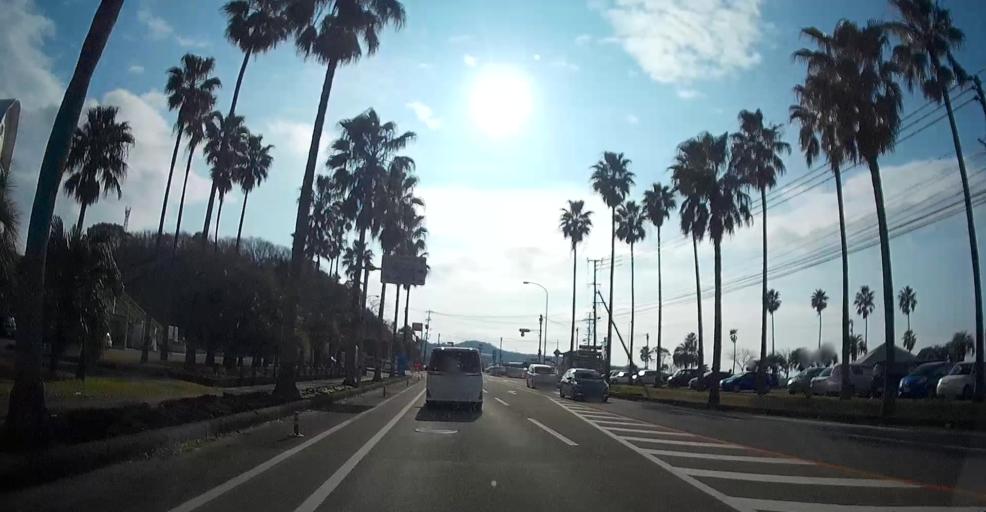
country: JP
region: Kumamoto
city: Yatsushiro
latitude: 32.5765
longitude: 130.4207
